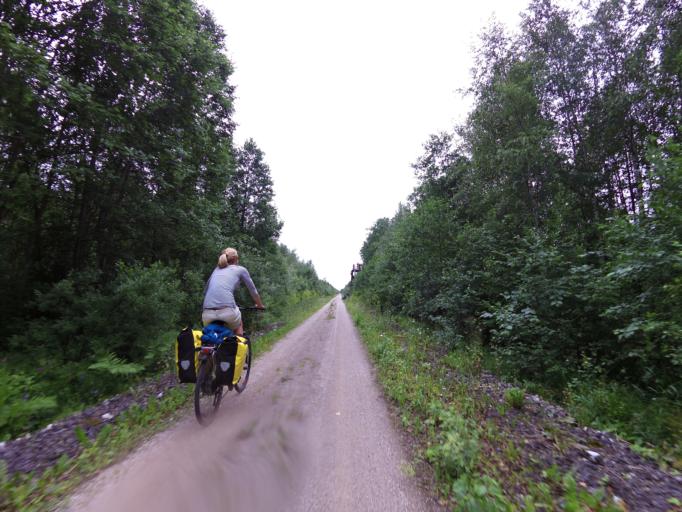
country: EE
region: Harju
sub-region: Nissi vald
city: Turba
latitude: 59.0153
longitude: 24.0890
